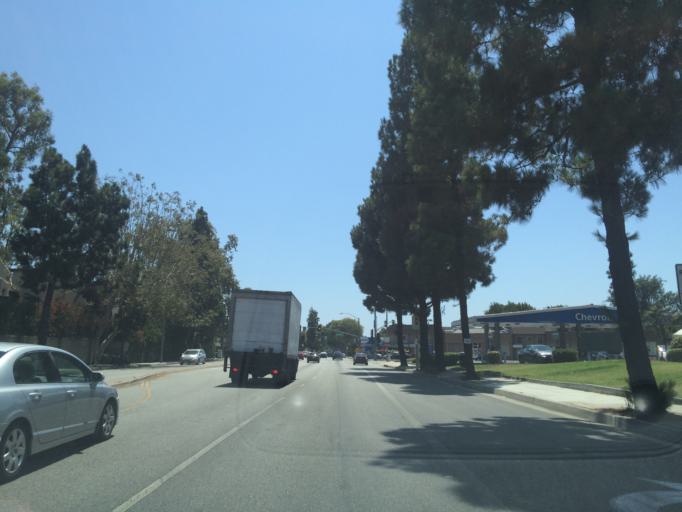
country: US
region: California
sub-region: Los Angeles County
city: Culver City
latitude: 34.0053
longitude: -118.3930
